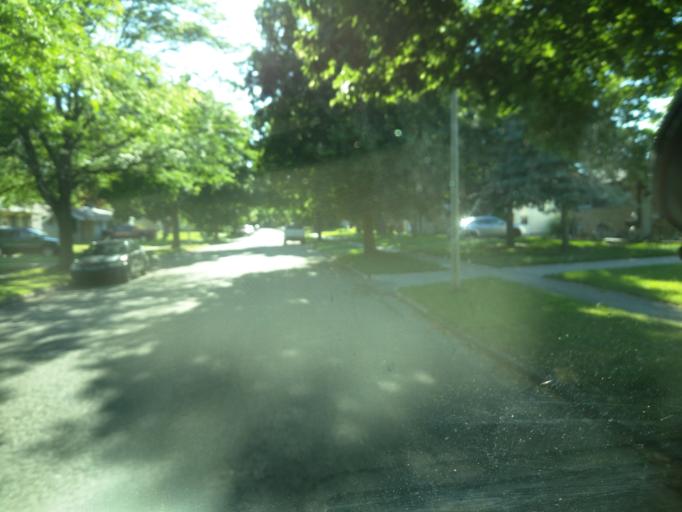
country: US
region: Michigan
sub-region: Eaton County
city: Waverly
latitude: 42.6874
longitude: -84.5990
